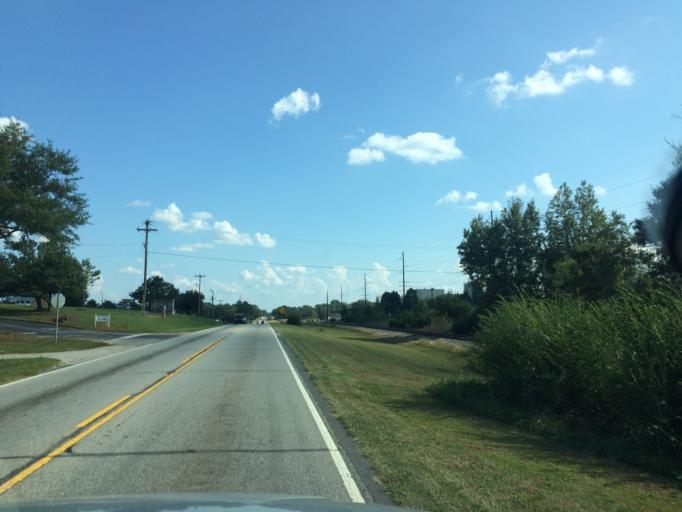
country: US
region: South Carolina
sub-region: Greenville County
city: Fountain Inn
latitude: 34.6201
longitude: -82.1244
